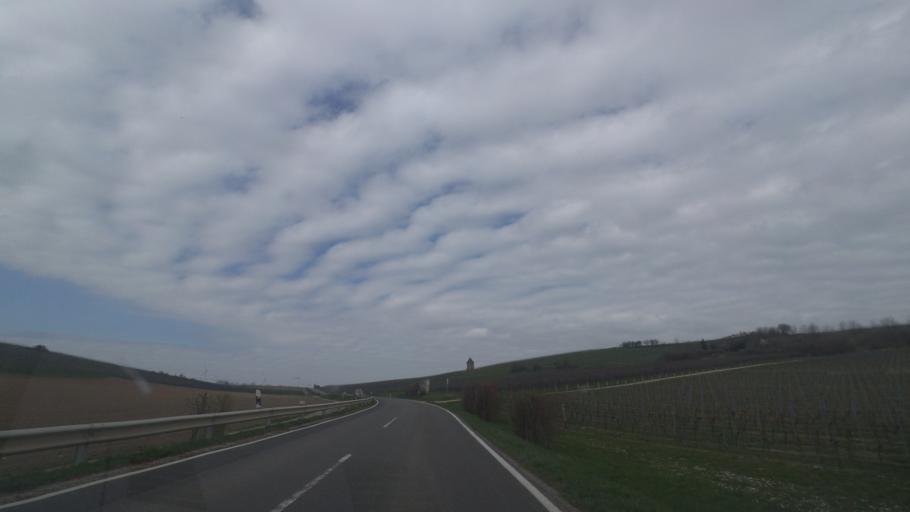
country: DE
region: Rheinland-Pfalz
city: Alzey
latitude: 49.7504
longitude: 8.0969
